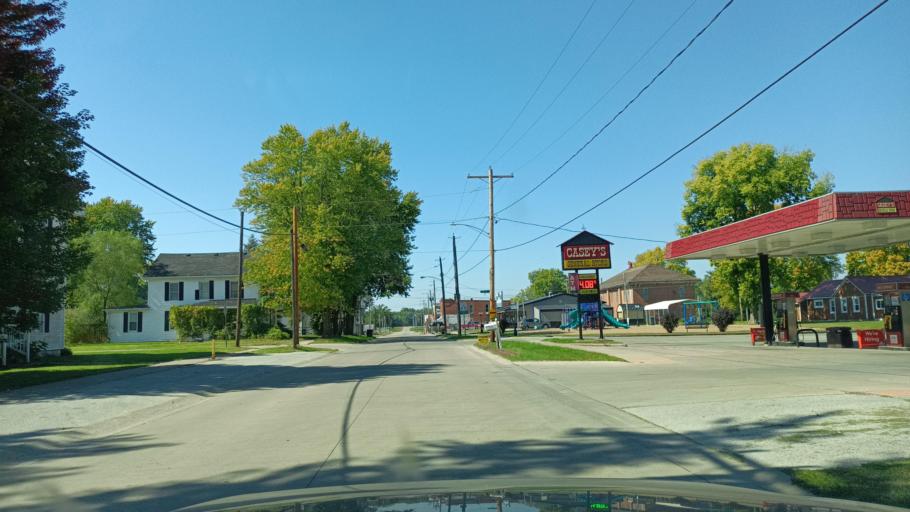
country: US
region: Illinois
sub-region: Henderson County
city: Oquawka
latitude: 41.1006
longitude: -90.9402
